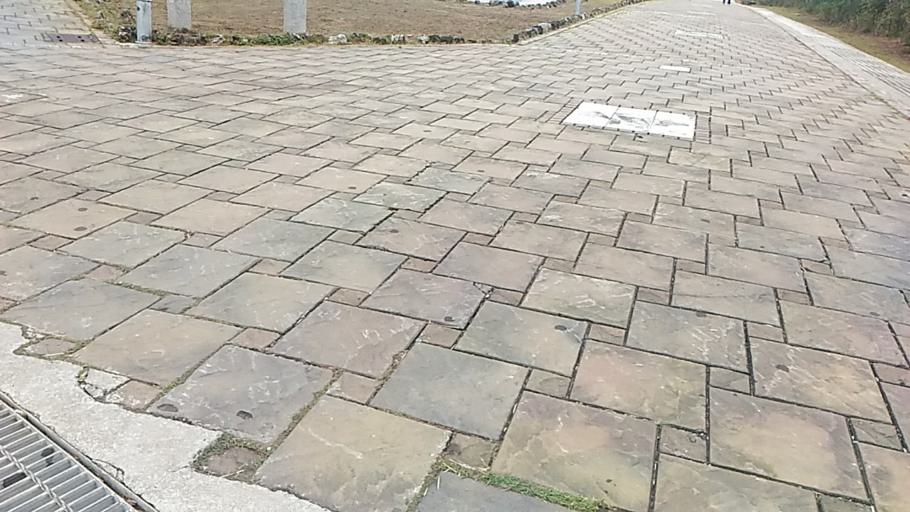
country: TW
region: Taiwan
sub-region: Penghu
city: Ma-kung
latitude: 23.3694
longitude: 119.4951
